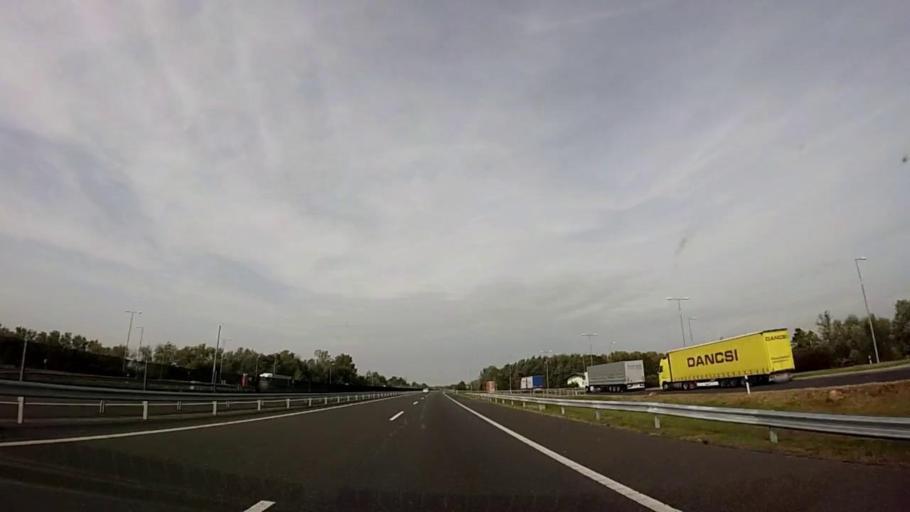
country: HU
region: Somogy
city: Balatonfenyves
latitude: 46.6995
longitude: 17.5141
